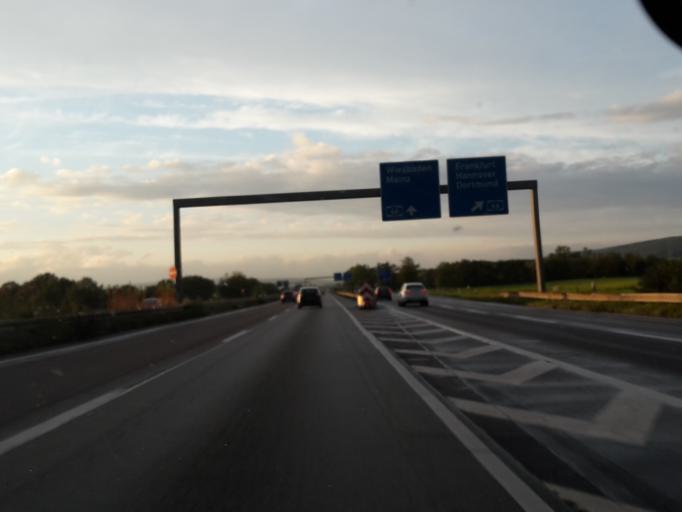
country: DE
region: Hesse
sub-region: Regierungsbezirk Darmstadt
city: Florsheim
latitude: 50.0519
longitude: 8.3912
